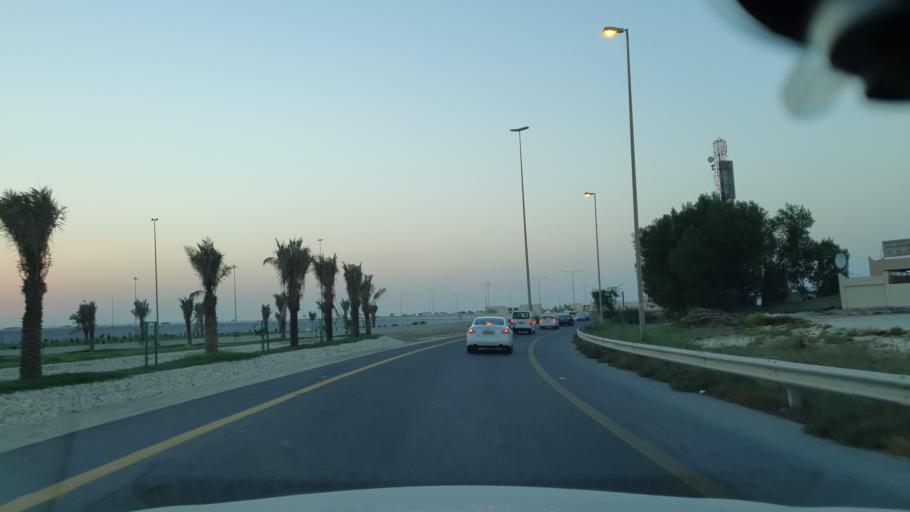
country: BH
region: Central Governorate
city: Madinat Hamad
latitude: 26.1733
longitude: 50.4684
